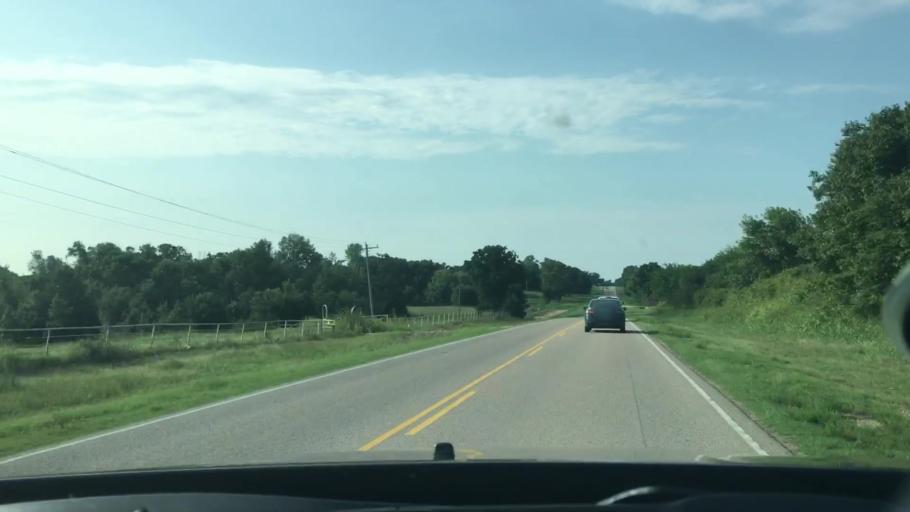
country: US
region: Oklahoma
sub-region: Johnston County
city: Tishomingo
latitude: 34.2665
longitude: -96.6711
